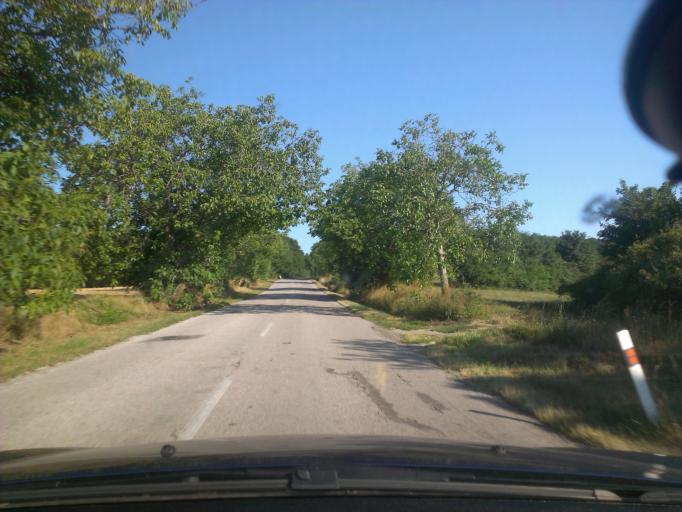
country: SK
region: Trnavsky
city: Vrbove
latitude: 48.6564
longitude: 17.6994
